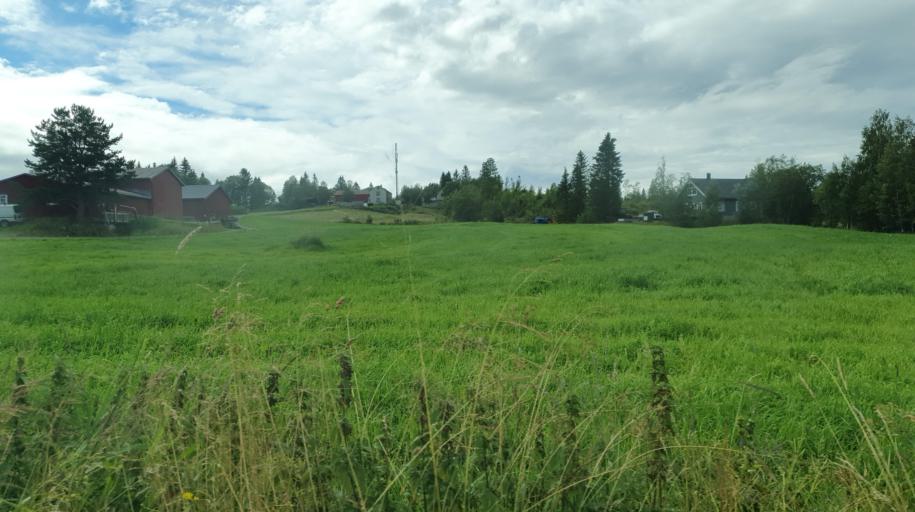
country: NO
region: Nord-Trondelag
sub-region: Levanger
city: Skogn
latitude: 63.5546
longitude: 11.1678
